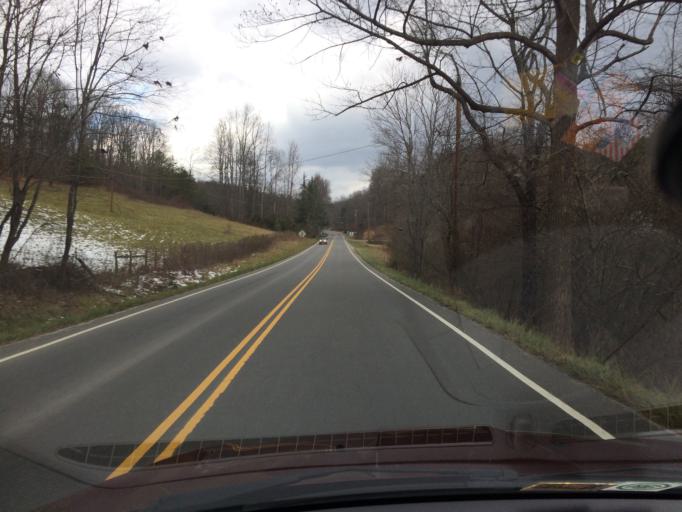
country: US
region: Virginia
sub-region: Patrick County
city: Stuart
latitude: 36.7227
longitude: -80.2388
